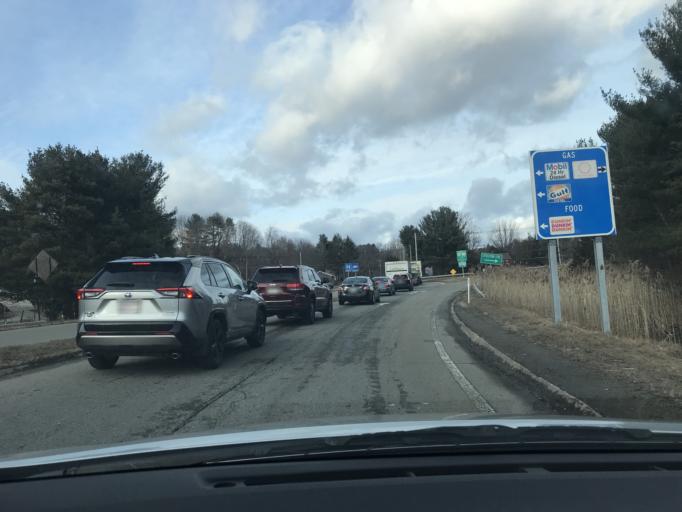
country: US
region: Massachusetts
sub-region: Middlesex County
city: Littleton Common
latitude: 42.5390
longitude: -71.4956
